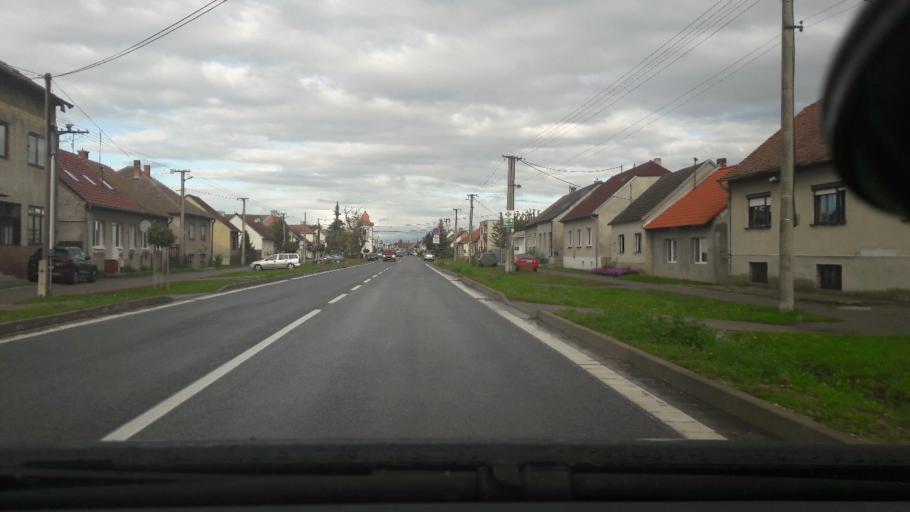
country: CZ
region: South Moravian
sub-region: Okres Breclav
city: Lanzhot
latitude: 48.6543
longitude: 17.0145
